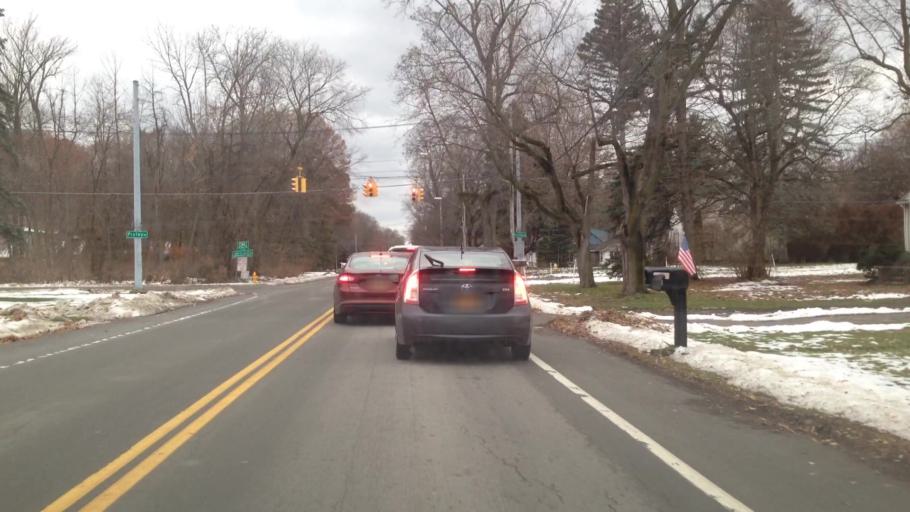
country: US
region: New York
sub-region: Monroe County
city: North Gates
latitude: 43.1257
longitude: -77.7101
